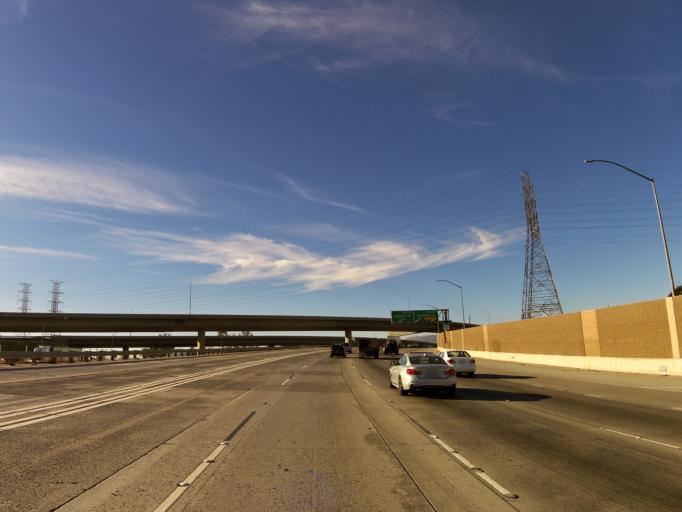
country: US
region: California
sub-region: Los Angeles County
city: San Fernando
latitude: 34.2322
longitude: -118.4074
